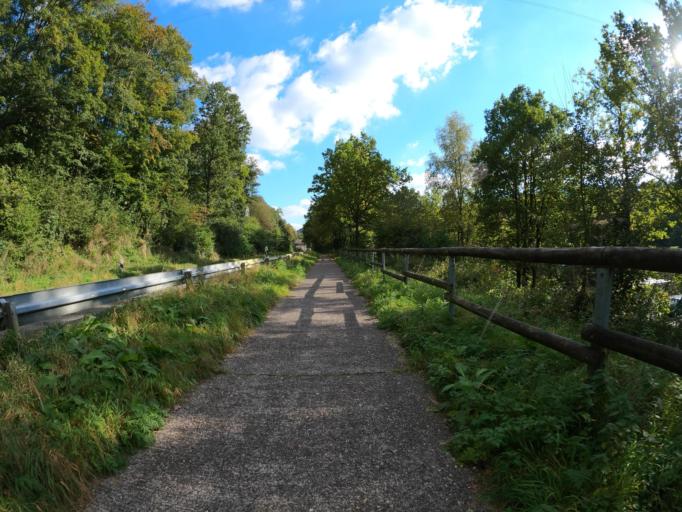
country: DE
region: North Rhine-Westphalia
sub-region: Regierungsbezirk Arnsberg
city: Schwelm
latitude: 51.2434
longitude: 7.3037
